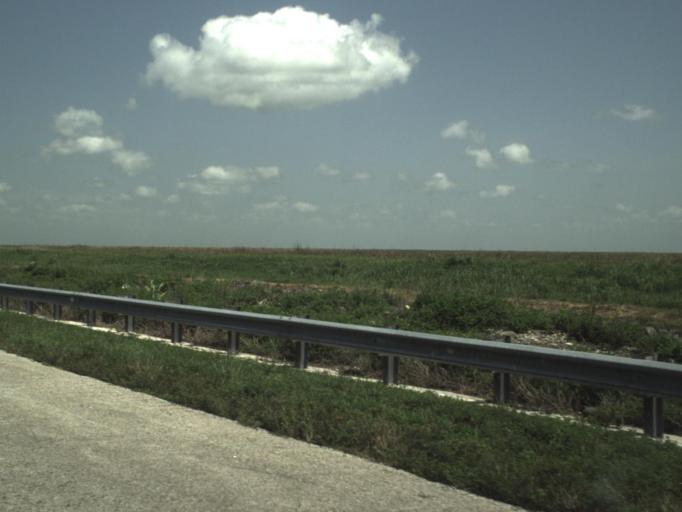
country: US
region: Florida
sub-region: Palm Beach County
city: Belle Glade Camp
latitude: 26.4105
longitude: -80.5961
